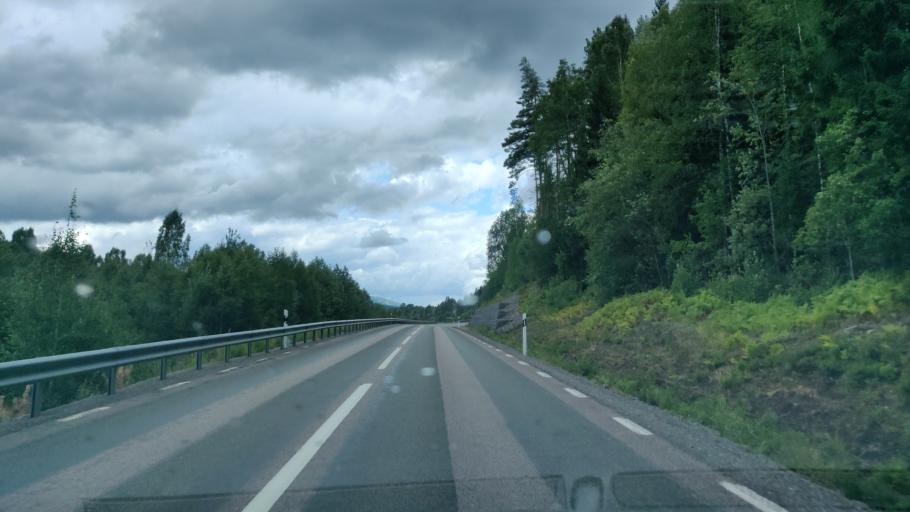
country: SE
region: Vaermland
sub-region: Torsby Kommun
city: Torsby
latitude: 60.5474
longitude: 13.1163
